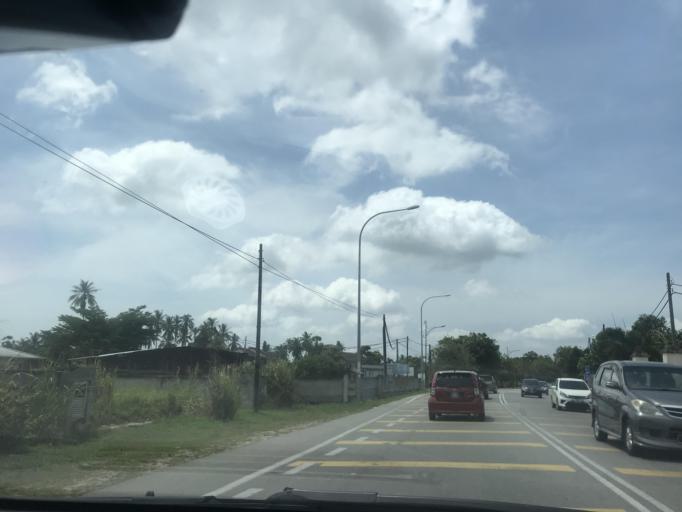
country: MY
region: Kelantan
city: Tumpat
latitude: 6.1774
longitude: 102.1793
